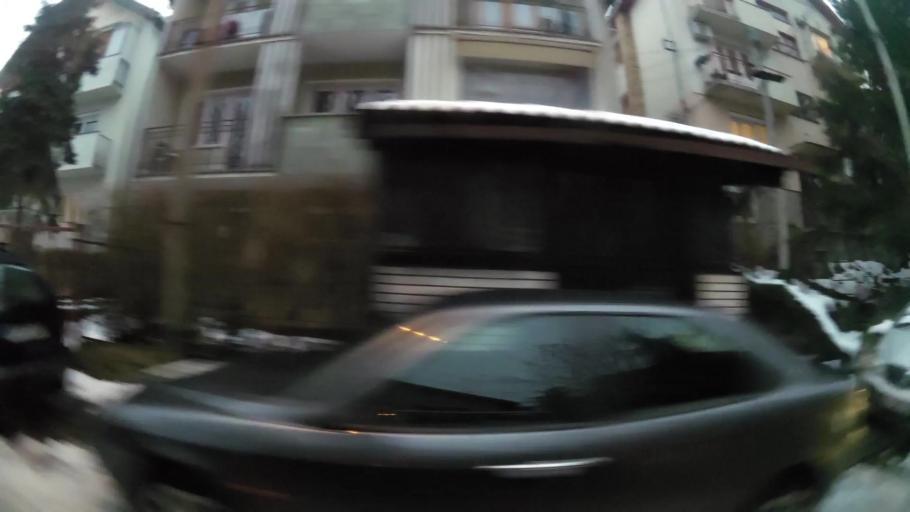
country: RS
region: Central Serbia
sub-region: Belgrade
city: Rakovica
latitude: 44.7555
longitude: 20.4264
